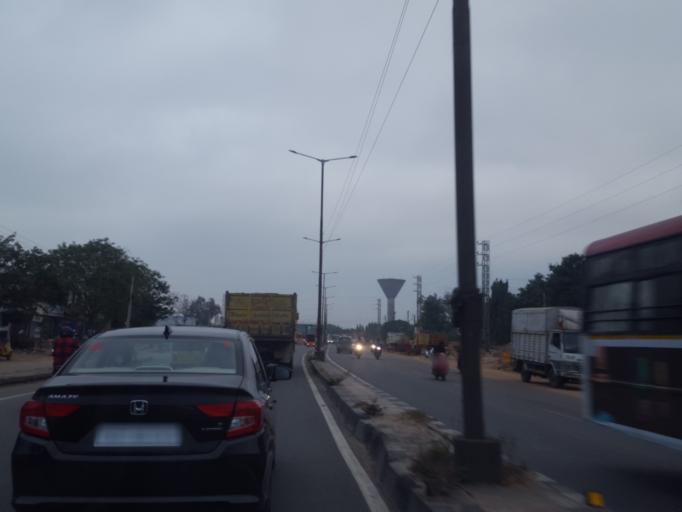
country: IN
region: Telangana
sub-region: Medak
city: Patancheru
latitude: 17.5213
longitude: 78.2760
